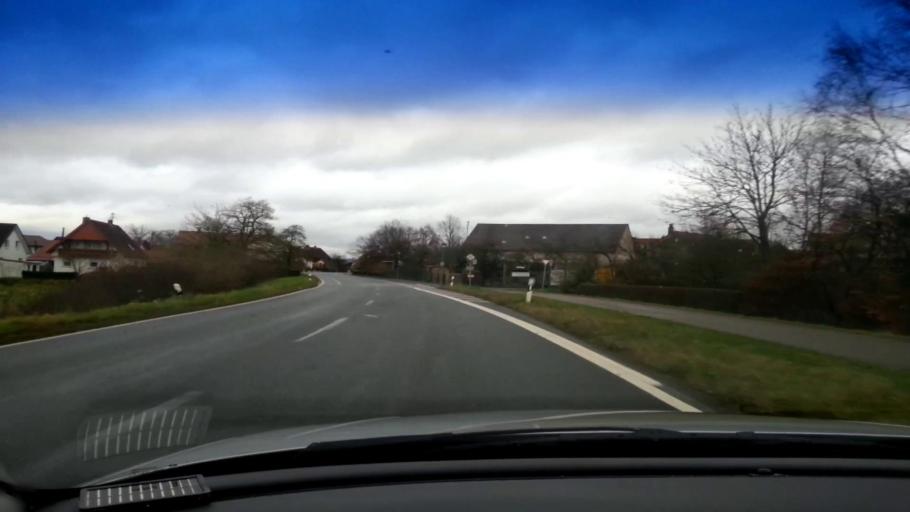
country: DE
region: Bavaria
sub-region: Upper Franconia
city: Zapfendorf
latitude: 50.0358
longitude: 10.9436
